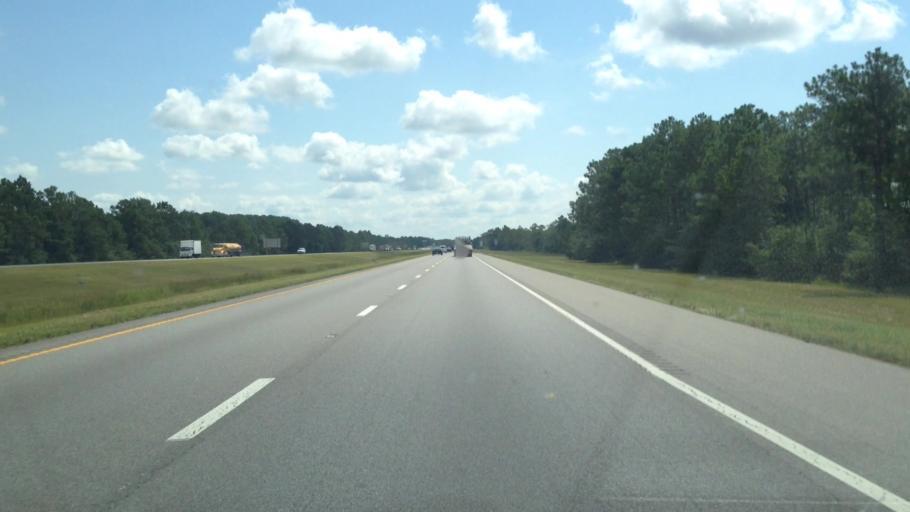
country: US
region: Mississippi
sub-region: Jackson County
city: Hickory Hills
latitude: 30.4353
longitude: -88.6500
